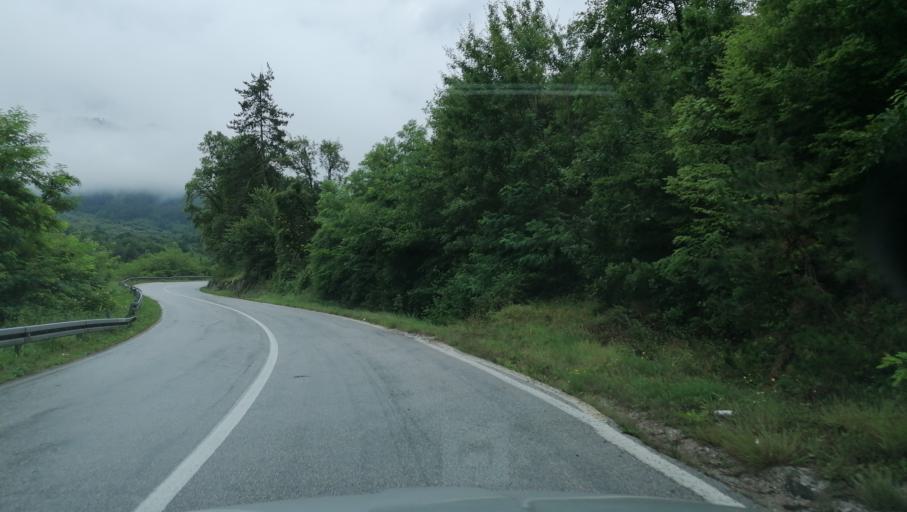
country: BA
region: Republika Srpska
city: Visegrad
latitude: 43.7868
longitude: 19.3249
